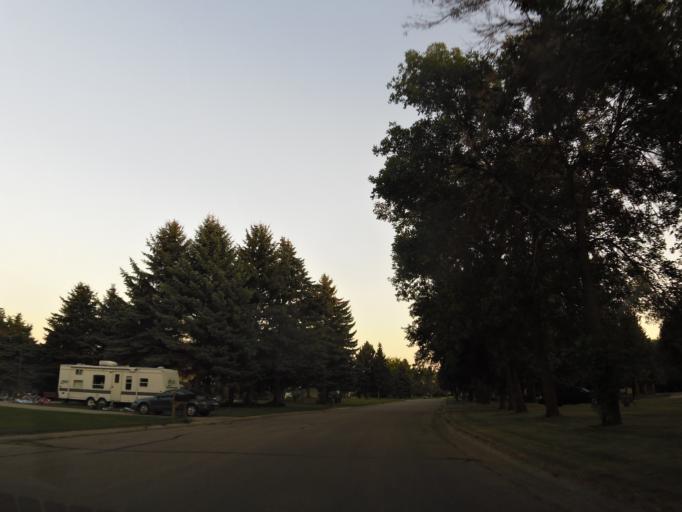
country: US
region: North Dakota
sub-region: Grand Forks County
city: Grand Forks
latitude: 47.8560
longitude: -97.0090
